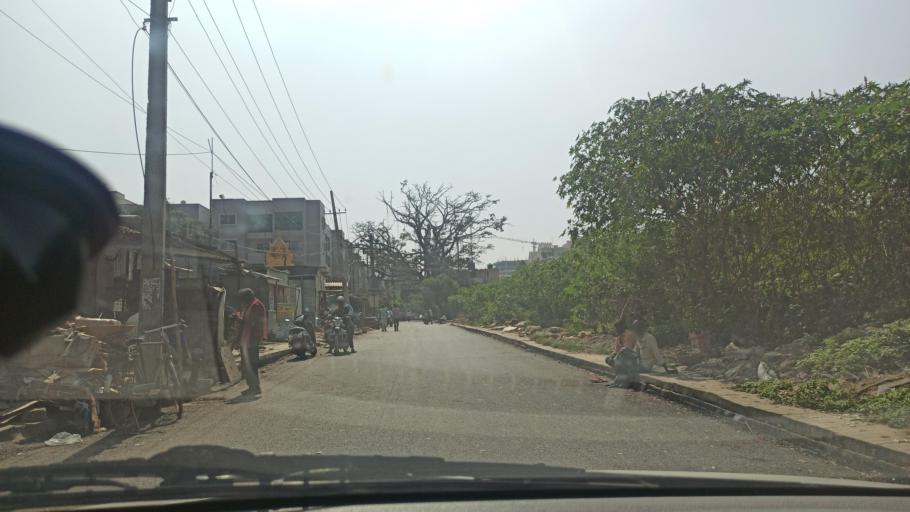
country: IN
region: Karnataka
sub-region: Bangalore Urban
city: Bangalore
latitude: 12.9359
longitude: 77.6864
